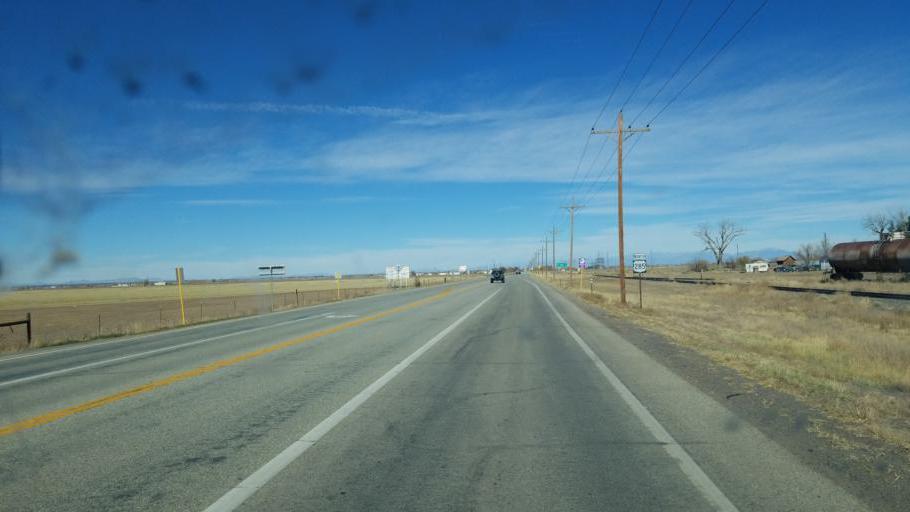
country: US
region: Colorado
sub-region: Conejos County
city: Conejos
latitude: 37.1748
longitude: -105.9876
